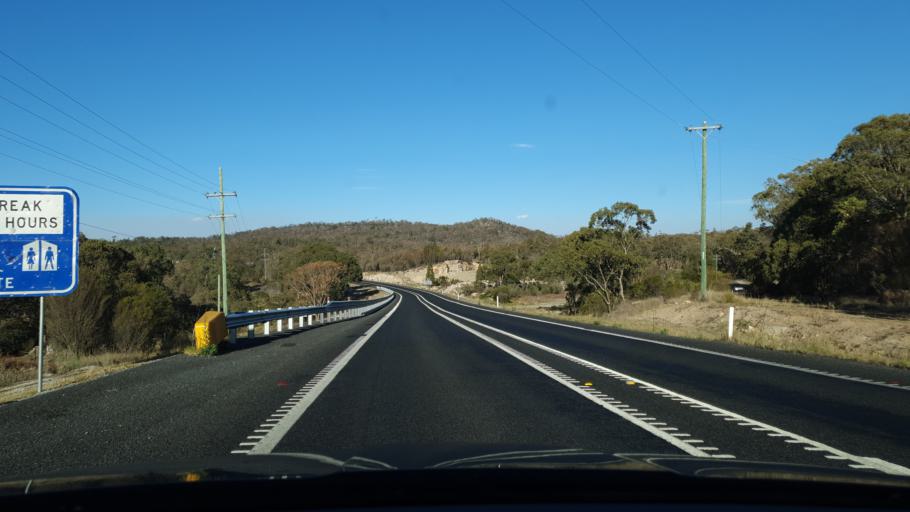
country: AU
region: Queensland
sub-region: Southern Downs
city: Stanthorpe
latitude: -28.6846
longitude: 151.9148
